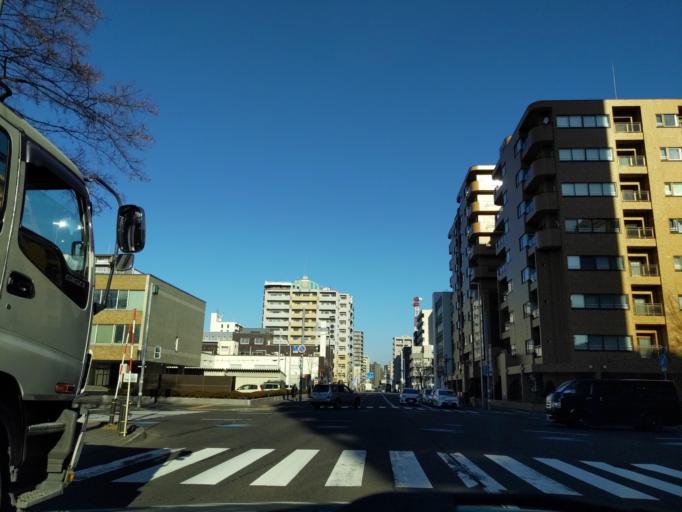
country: JP
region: Hokkaido
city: Sapporo
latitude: 43.0618
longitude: 141.3340
